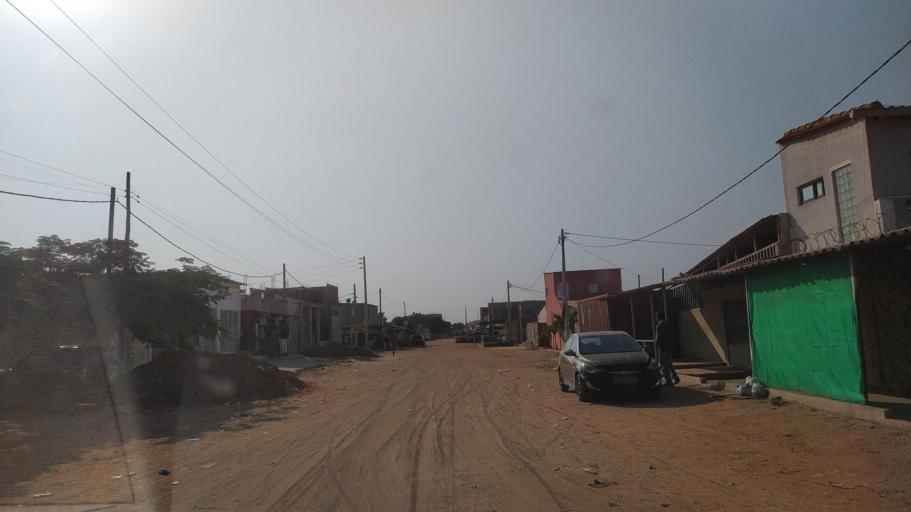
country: AO
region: Luanda
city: Luanda
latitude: -8.9348
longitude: 13.2530
